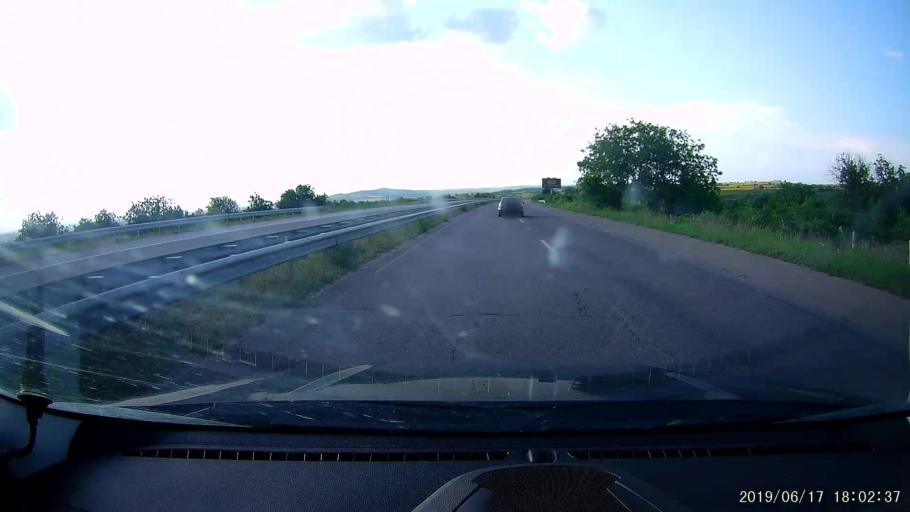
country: BG
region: Khaskovo
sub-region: Obshtina Svilengrad
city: Svilengrad
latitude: 41.7628
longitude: 26.2283
